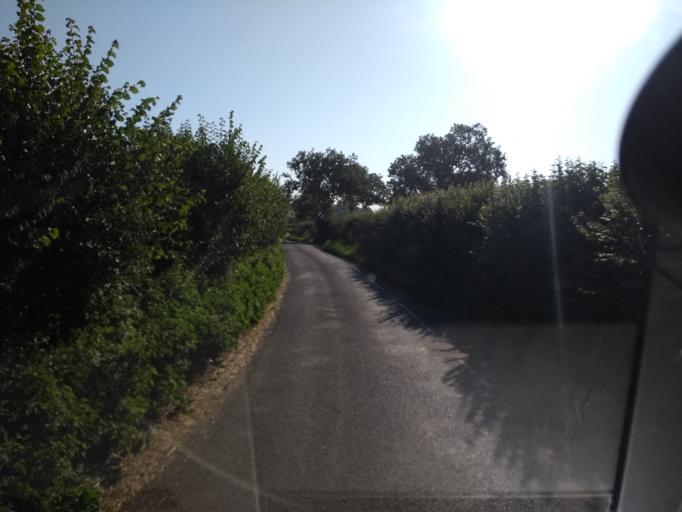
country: GB
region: England
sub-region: Somerset
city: Westonzoyland
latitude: 51.1355
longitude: -2.9383
